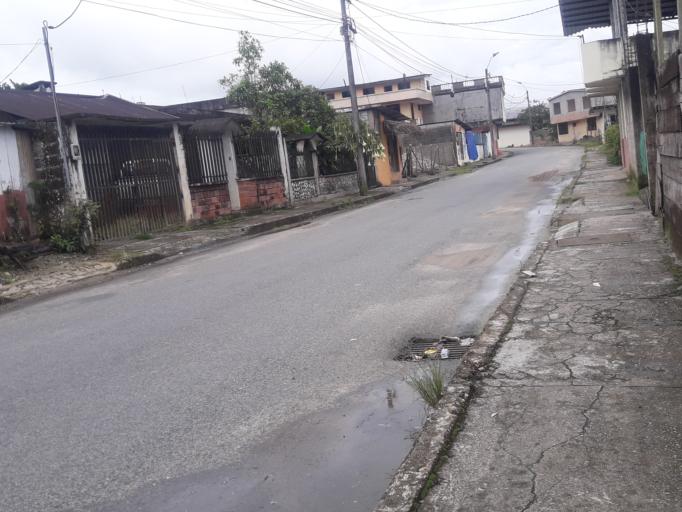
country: EC
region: Napo
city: Tena
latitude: -0.9965
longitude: -77.8086
